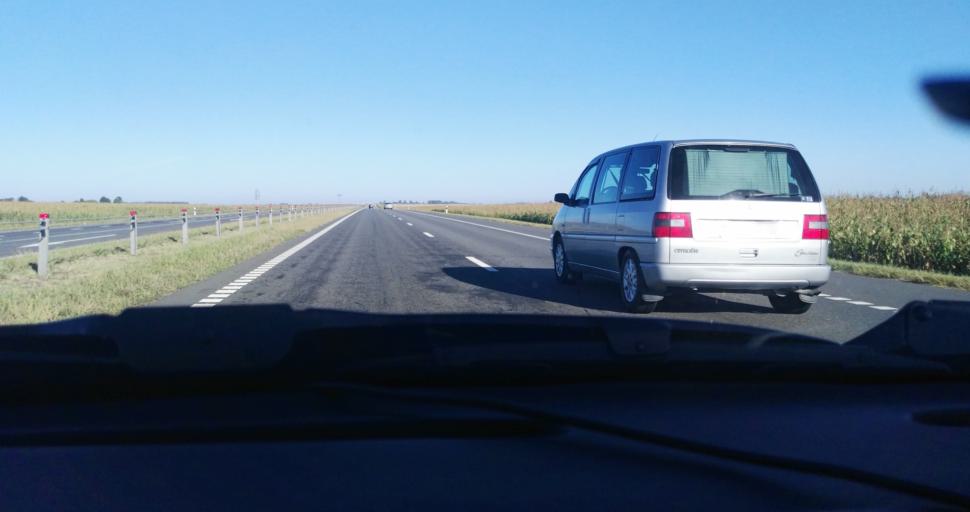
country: BY
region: Gomel
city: Buda-Kashalyova
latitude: 52.5247
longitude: 30.6185
